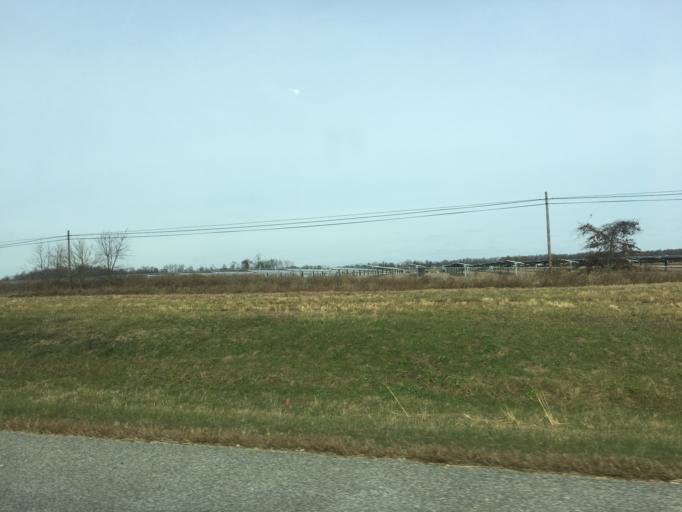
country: US
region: Maryland
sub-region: Queen Anne's County
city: Centreville
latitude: 38.9363
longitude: -76.0457
